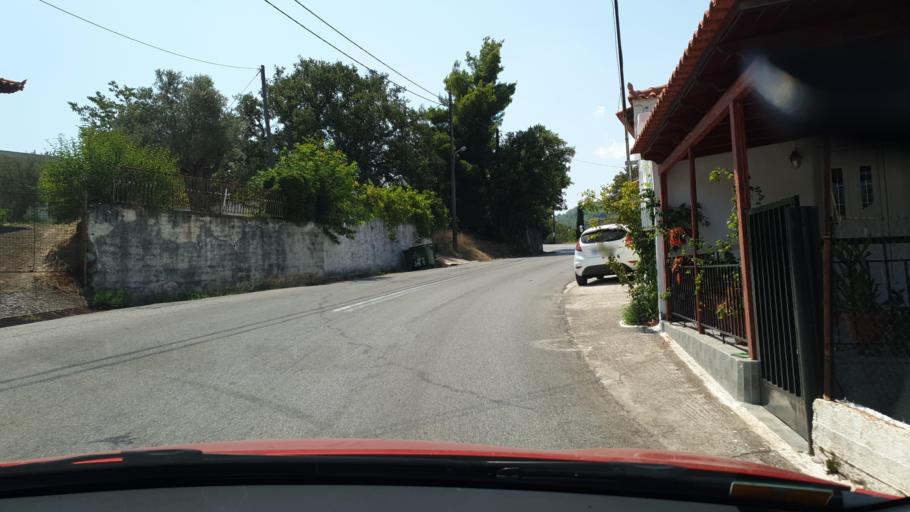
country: GR
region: Central Greece
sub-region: Nomos Evvoias
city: Oxilithos
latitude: 38.5412
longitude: 24.0761
